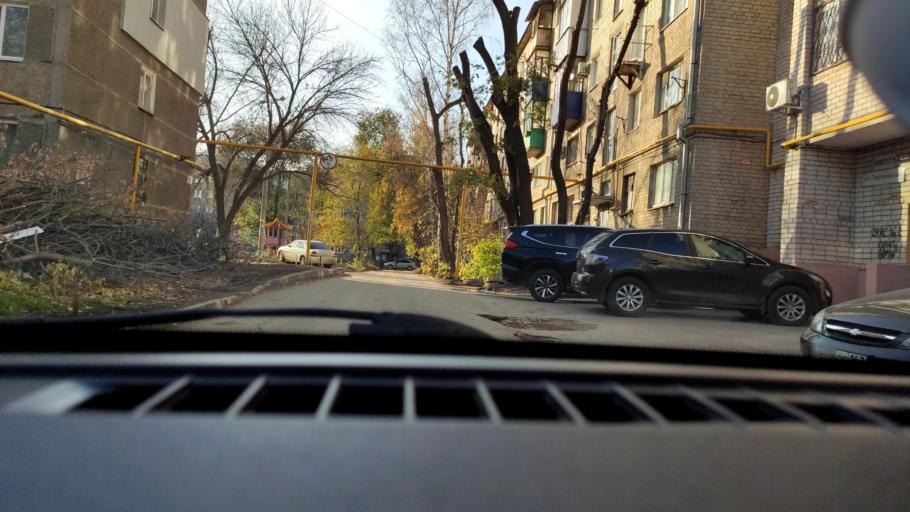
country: RU
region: Samara
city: Samara
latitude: 53.1869
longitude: 50.1960
